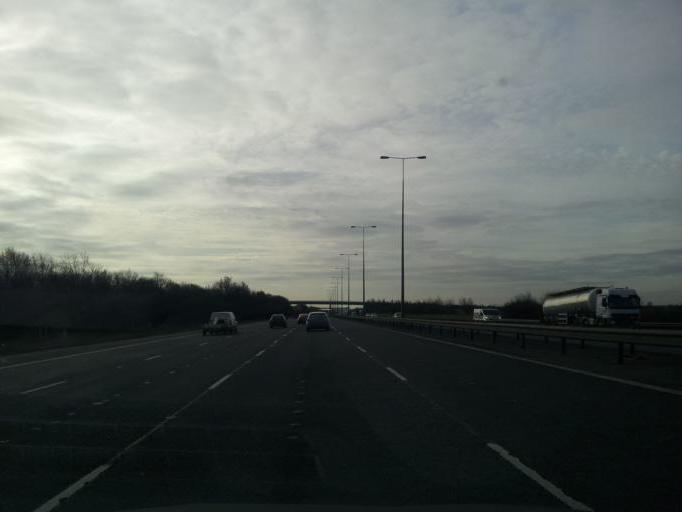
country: GB
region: England
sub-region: Cambridgeshire
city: Stilton
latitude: 52.4714
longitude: -0.2843
